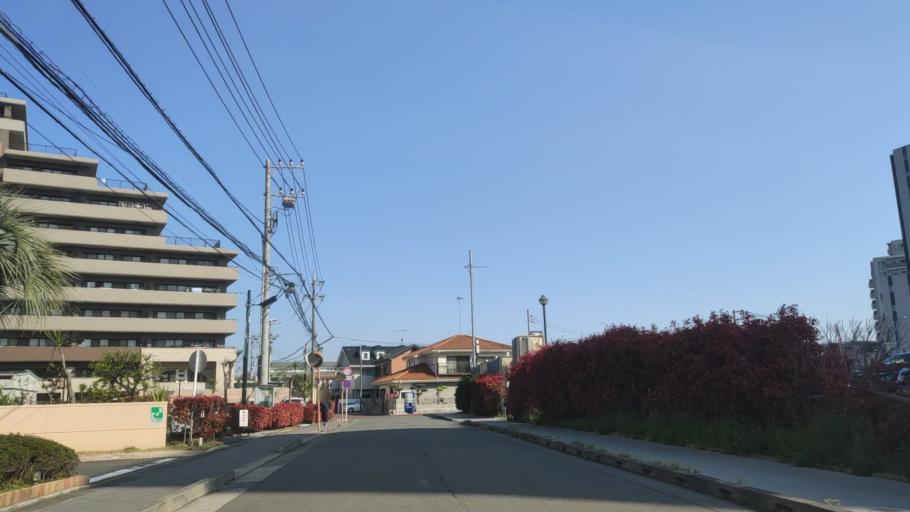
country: JP
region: Kanagawa
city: Fujisawa
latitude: 35.3410
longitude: 139.4439
